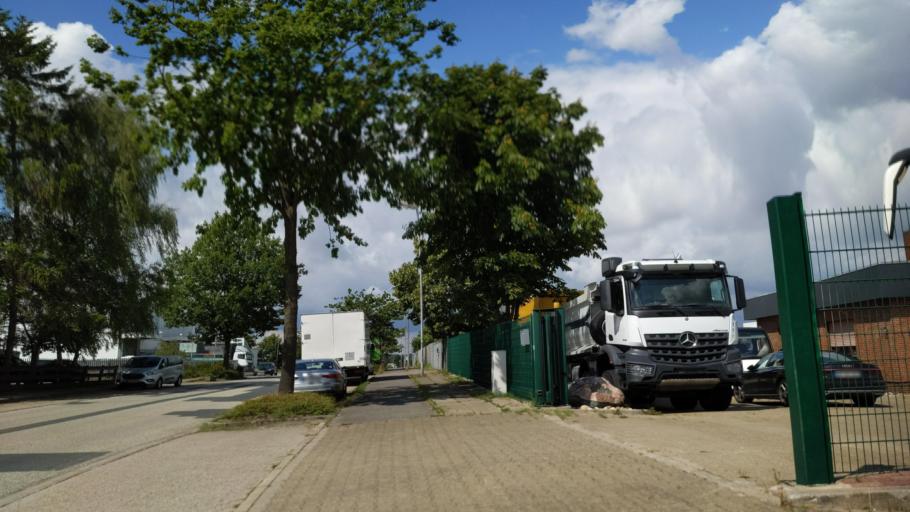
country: DE
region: Schleswig-Holstein
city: Reinfeld
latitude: 53.8290
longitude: 10.5030
